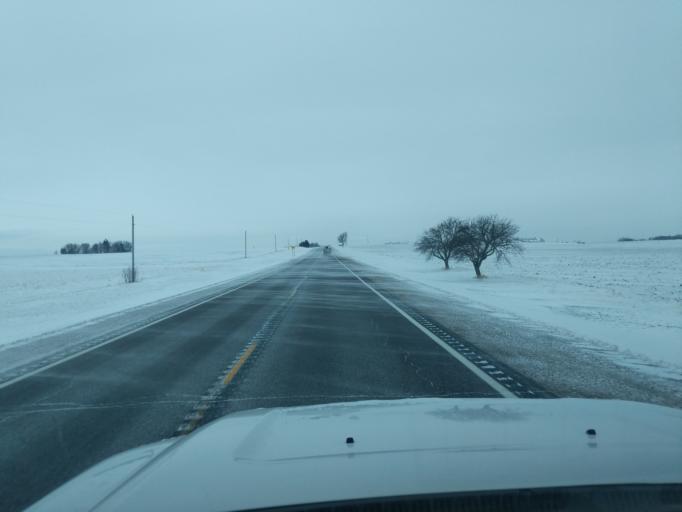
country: US
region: Minnesota
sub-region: Redwood County
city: Redwood Falls
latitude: 44.6121
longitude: -94.9946
